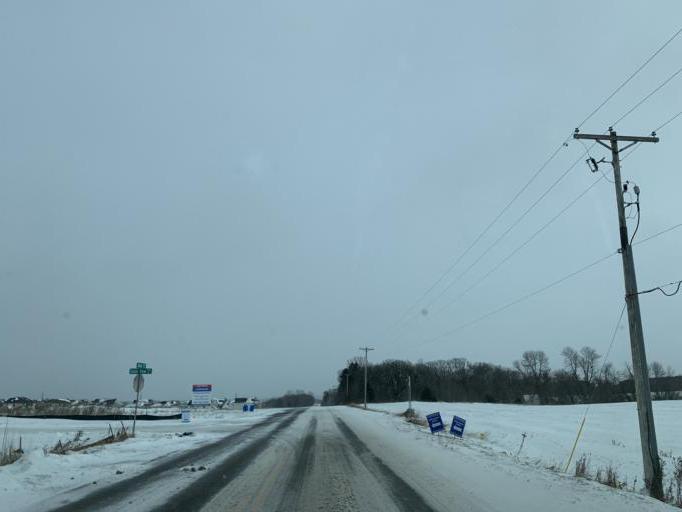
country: US
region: Minnesota
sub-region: Washington County
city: Cottage Grove
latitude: 44.8764
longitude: -92.9408
